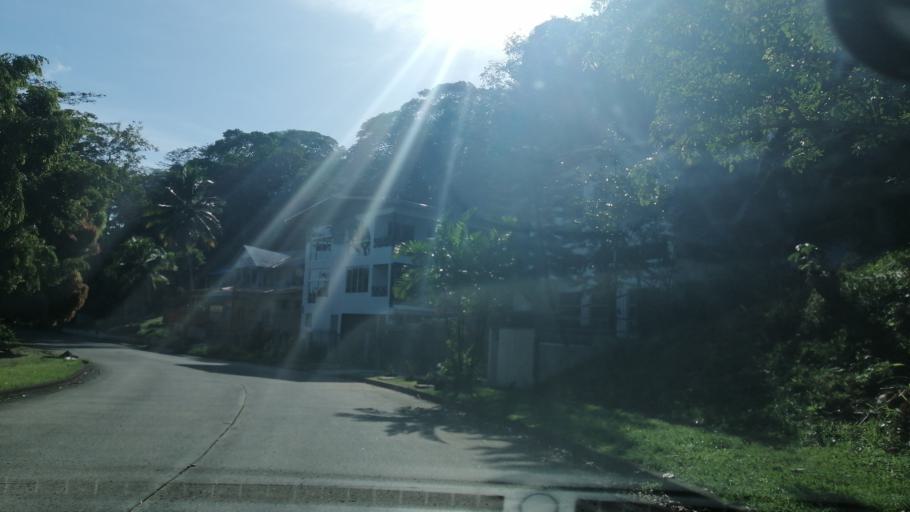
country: PA
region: Panama
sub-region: Distrito de Panama
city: Ancon
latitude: 8.9639
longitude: -79.5506
